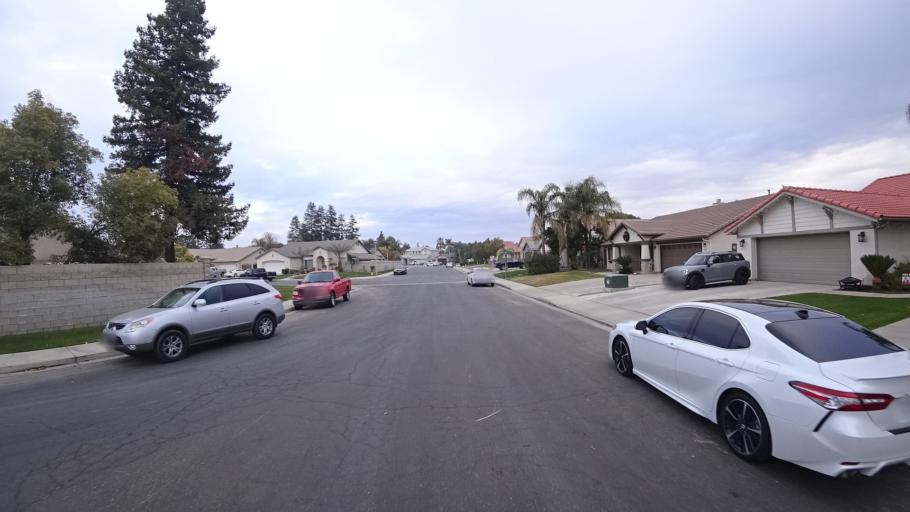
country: US
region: California
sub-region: Kern County
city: Greenfield
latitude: 35.3016
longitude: -119.0781
